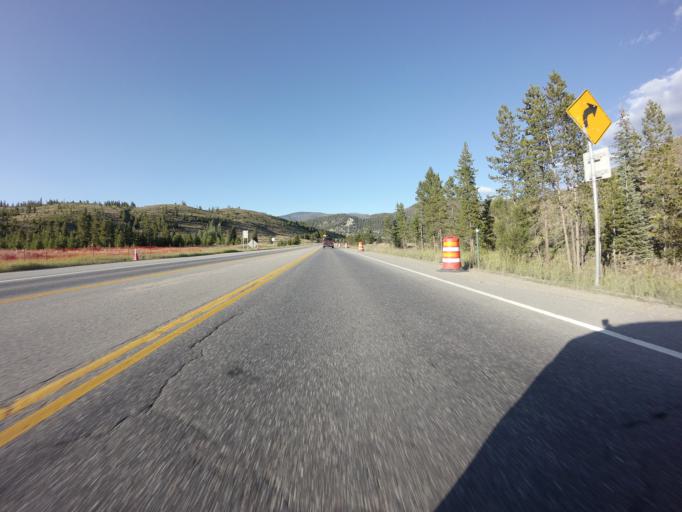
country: US
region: Colorado
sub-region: Summit County
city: Frisco
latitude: 39.5765
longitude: -106.0629
